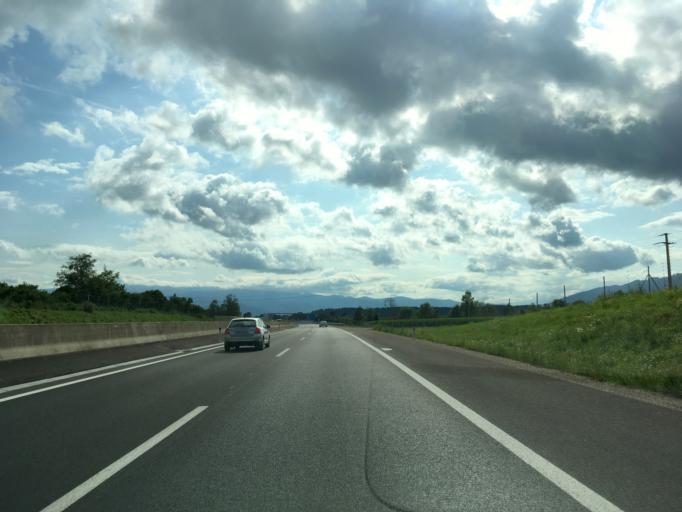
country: AT
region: Styria
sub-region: Politischer Bezirk Murtal
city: Knittelfeld
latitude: 47.2247
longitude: 14.8189
